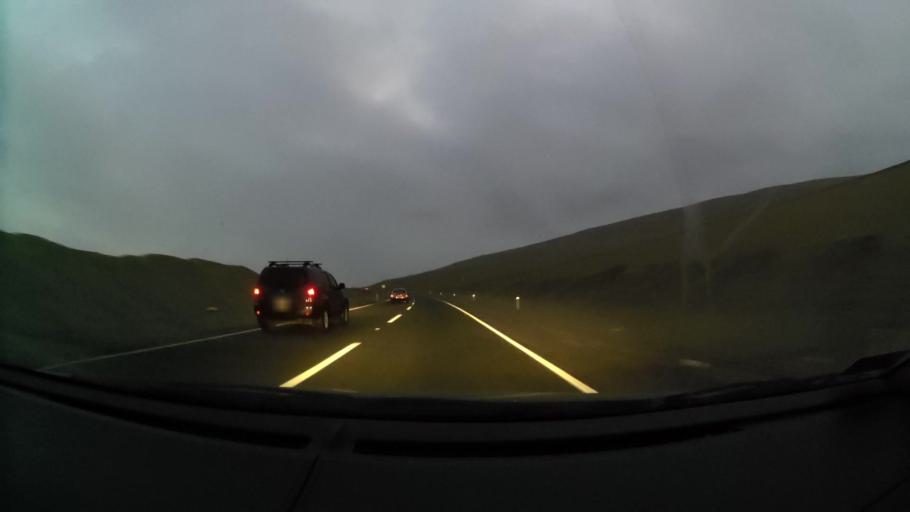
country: PE
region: Lima
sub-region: Lima
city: Santa Rosa
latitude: -11.7265
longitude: -77.1453
